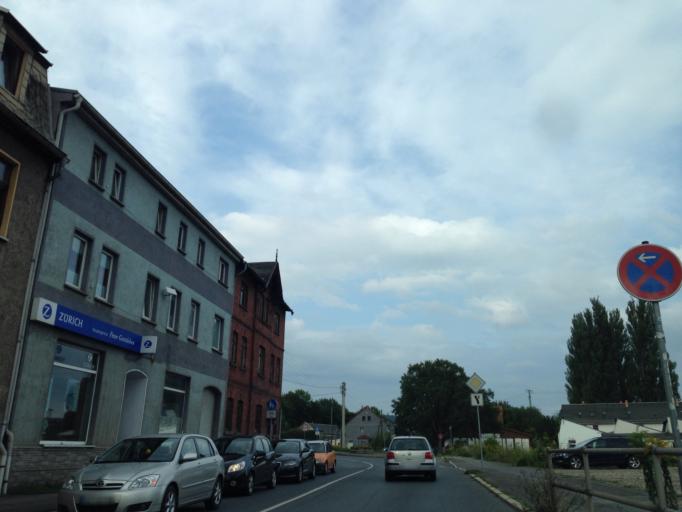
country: DE
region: Thuringia
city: Saalfeld
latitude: 50.6529
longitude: 11.3719
